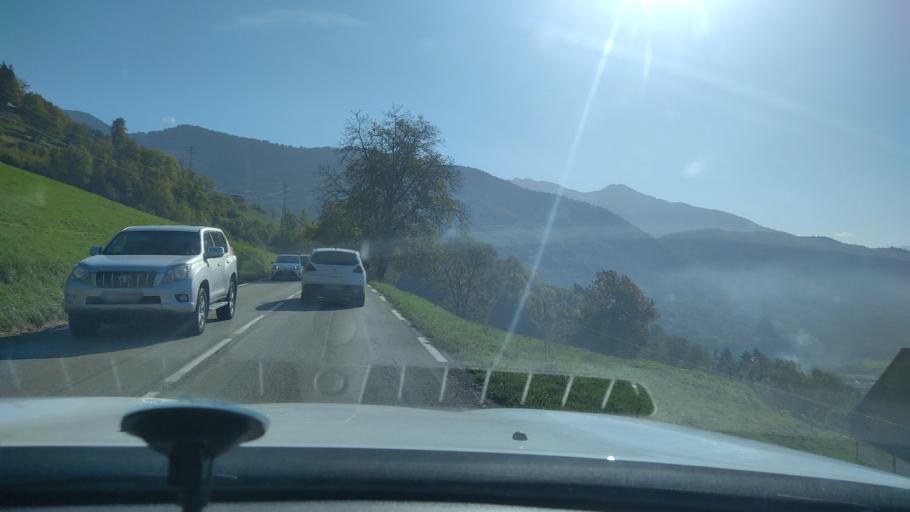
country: FR
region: Rhone-Alpes
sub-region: Departement de la Savoie
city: Ugine
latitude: 45.7601
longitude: 6.4253
